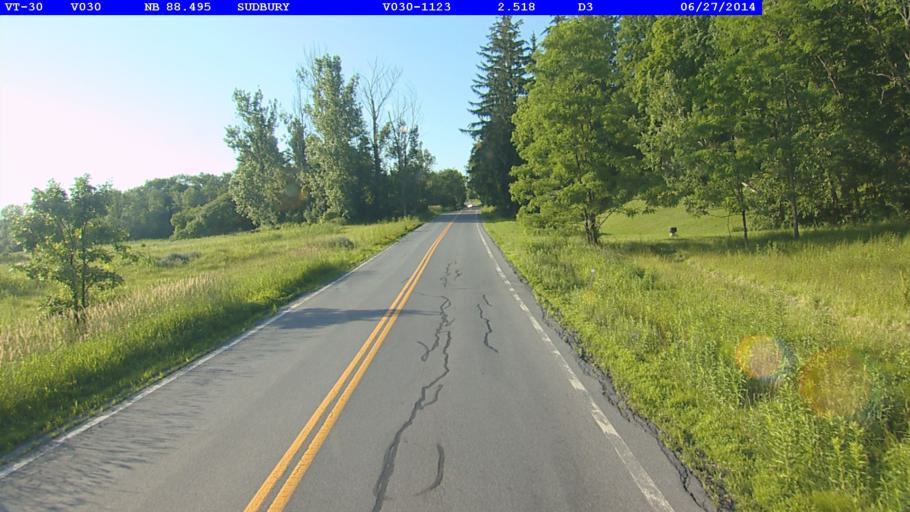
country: US
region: Vermont
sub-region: Rutland County
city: Brandon
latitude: 43.7843
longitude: -73.2030
